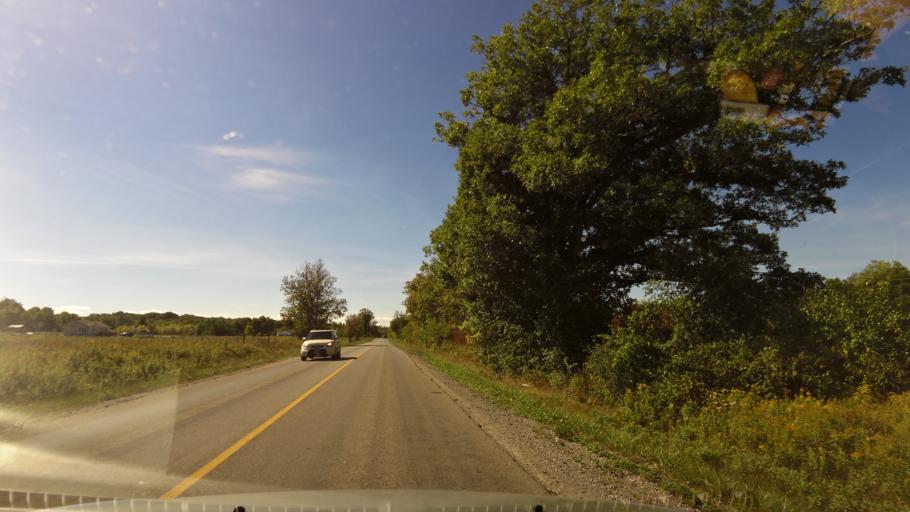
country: CA
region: Ontario
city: Ancaster
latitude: 43.0193
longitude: -80.0496
